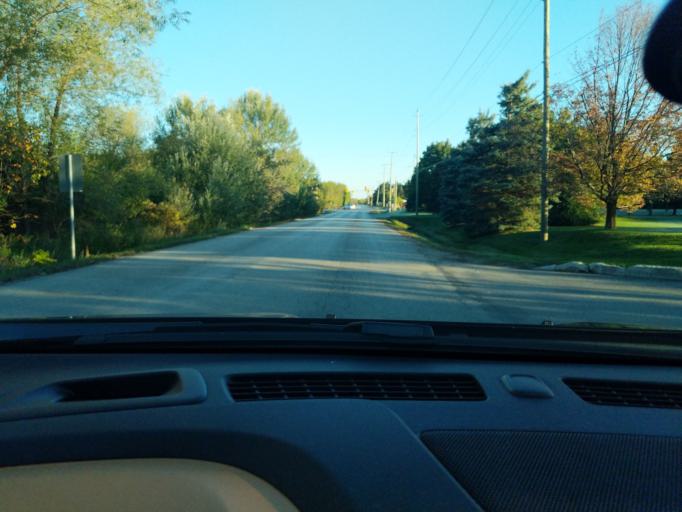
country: CA
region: Ontario
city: Collingwood
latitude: 44.4982
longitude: -80.2503
